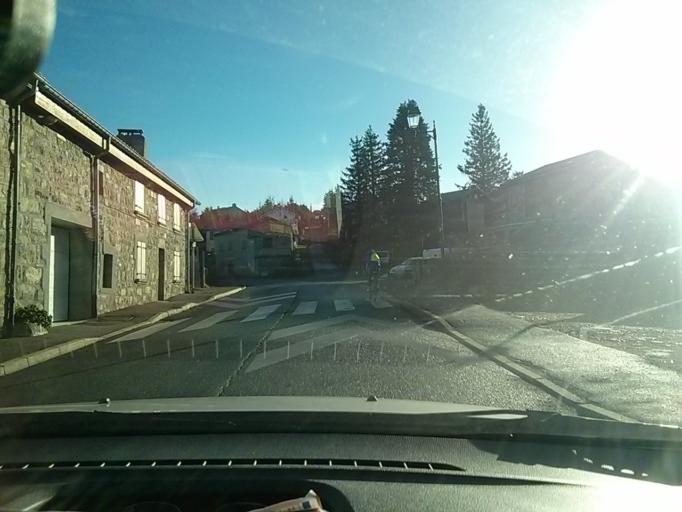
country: FR
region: Rhone-Alpes
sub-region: Departement de la Loire
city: Bourg-Argental
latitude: 45.3680
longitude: 4.5180
